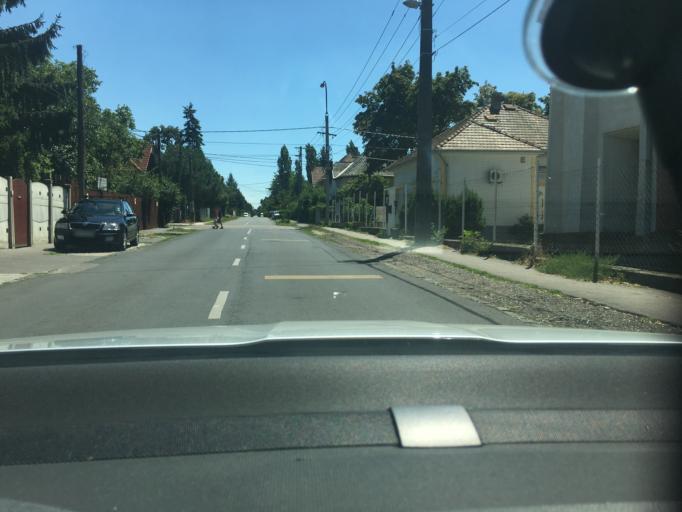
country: HU
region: Budapest
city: Budapest XVI. keruelet
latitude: 47.5219
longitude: 19.1595
